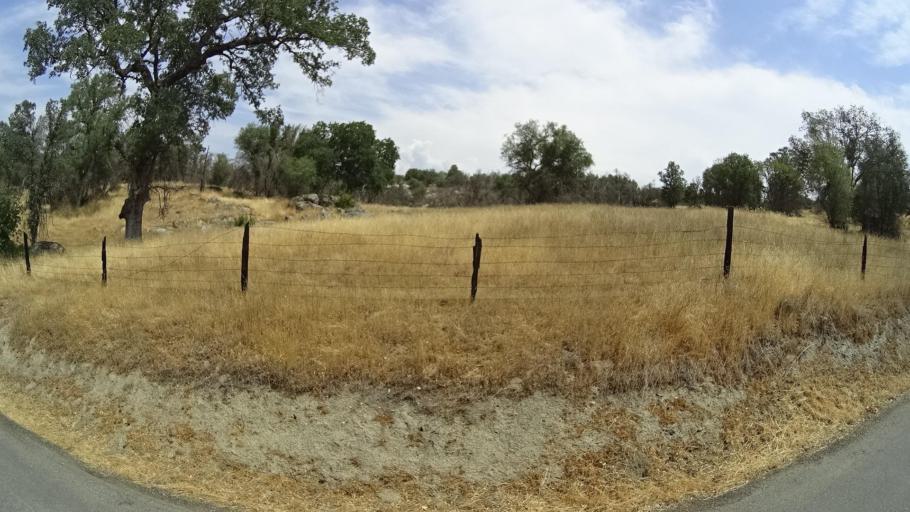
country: US
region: California
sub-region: Madera County
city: Ahwahnee
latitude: 37.3916
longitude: -119.8349
